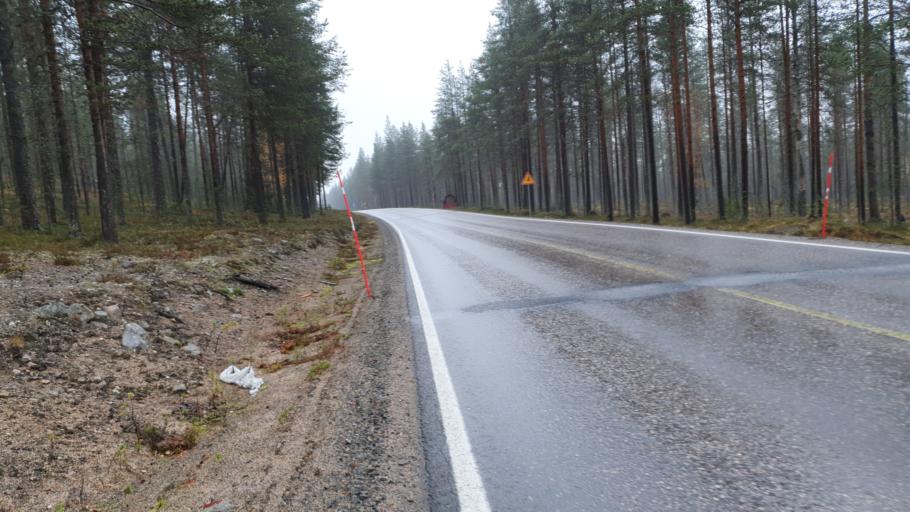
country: FI
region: Lapland
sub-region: Tunturi-Lappi
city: Kolari
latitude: 67.5956
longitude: 24.1156
